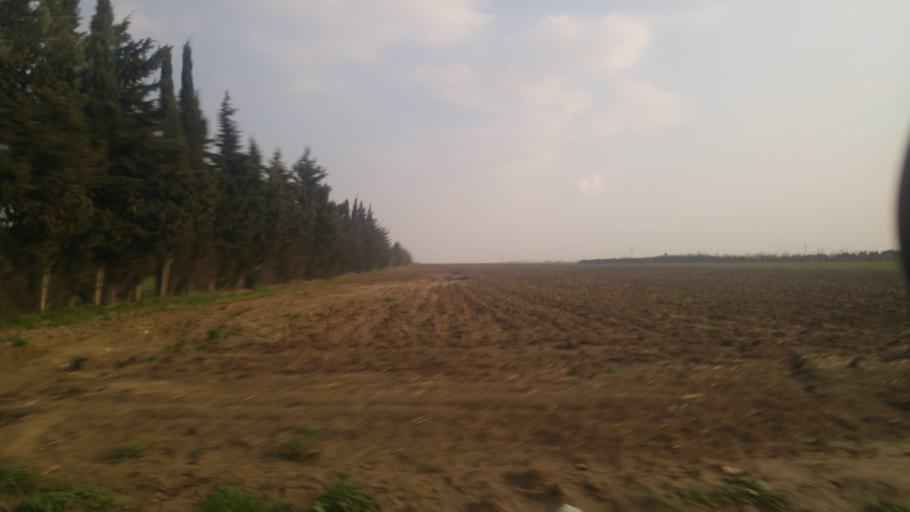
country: TR
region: Istanbul
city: Kavakli
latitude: 41.1125
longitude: 28.3012
